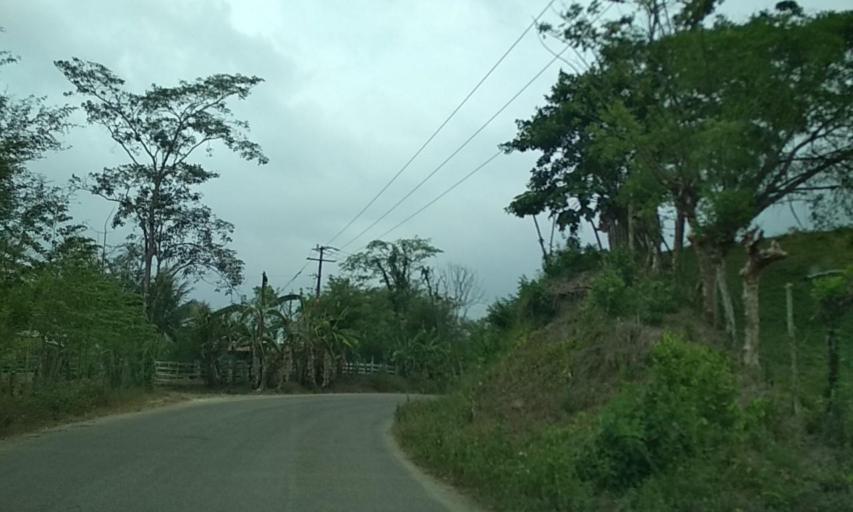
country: MX
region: Tabasco
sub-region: Huimanguillo
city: Francisco Rueda
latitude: 17.6039
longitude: -94.0930
